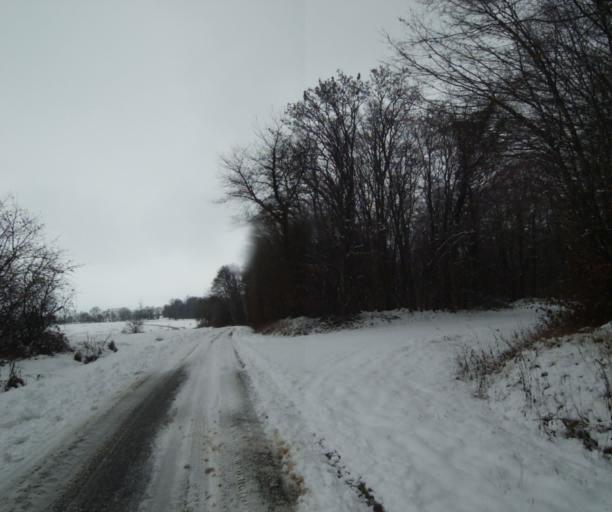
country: FR
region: Champagne-Ardenne
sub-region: Departement de la Haute-Marne
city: Wassy
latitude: 48.4524
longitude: 4.9464
